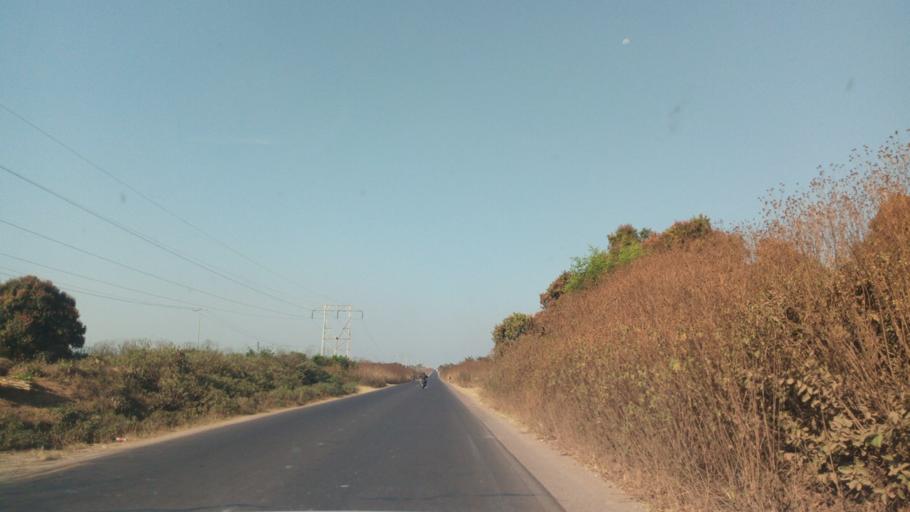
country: CD
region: Katanga
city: Likasi
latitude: -11.0026
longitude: 26.8519
